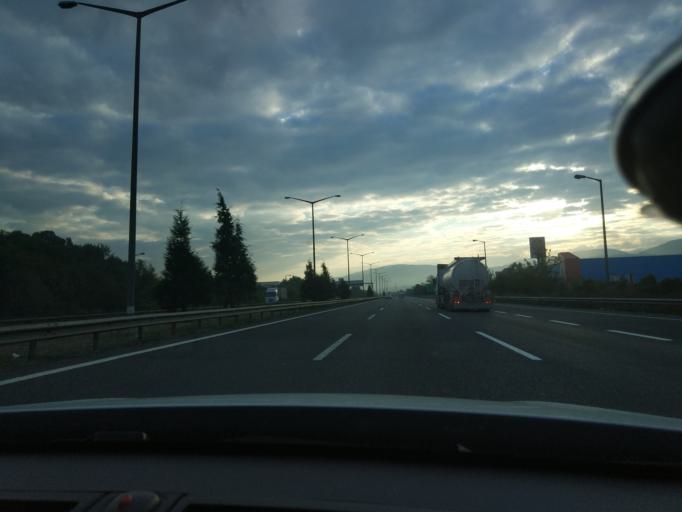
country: TR
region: Sakarya
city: Hendek
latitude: 40.7538
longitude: 30.7217
